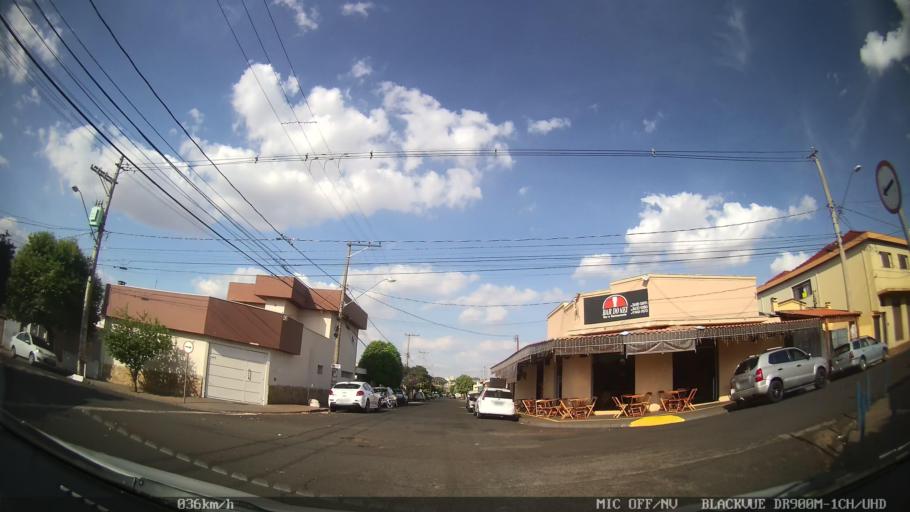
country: BR
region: Sao Paulo
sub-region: Ribeirao Preto
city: Ribeirao Preto
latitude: -21.1814
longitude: -47.8291
